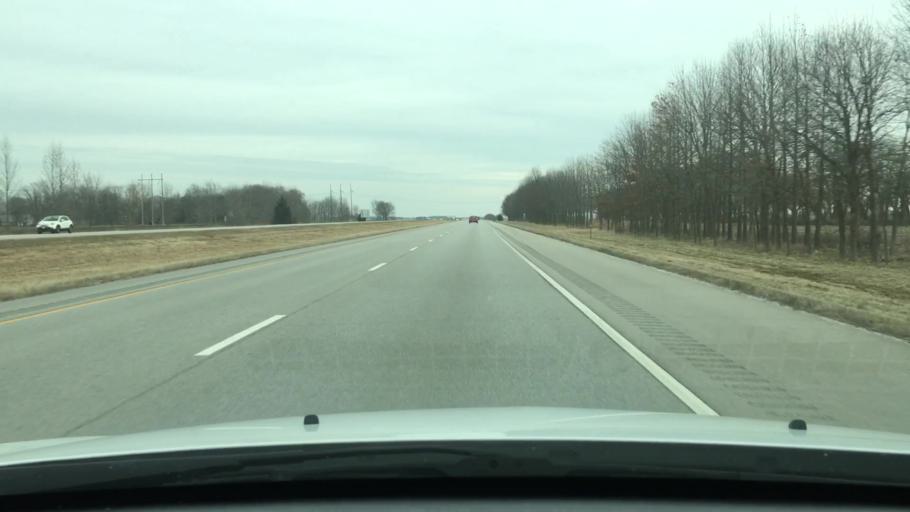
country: US
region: Illinois
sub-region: Sangamon County
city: New Berlin
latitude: 39.7368
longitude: -90.0206
